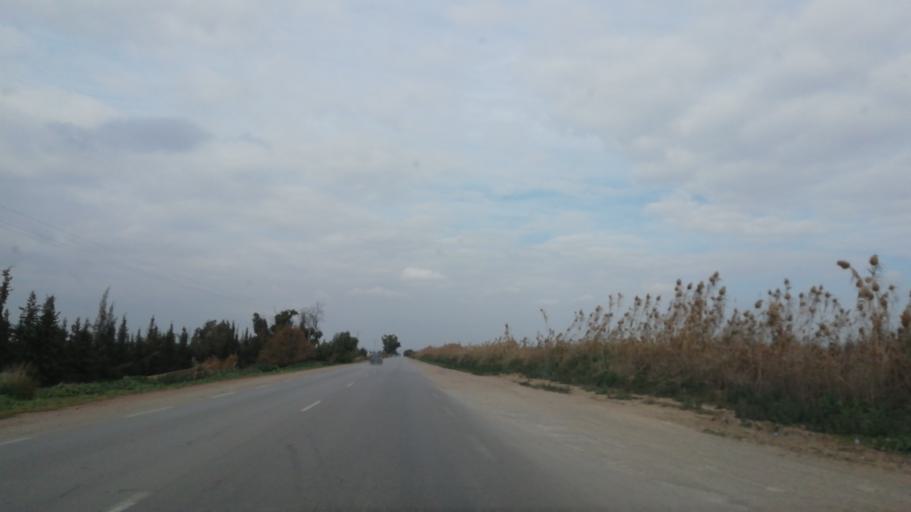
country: DZ
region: Mascara
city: Mascara
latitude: 35.6425
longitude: 0.0603
